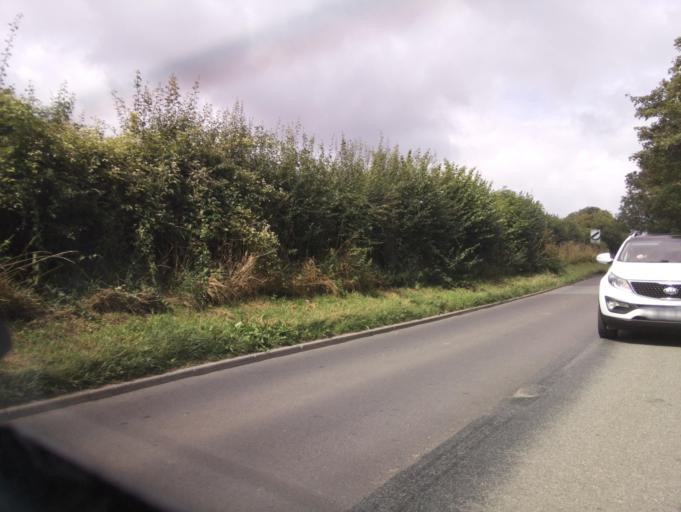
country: GB
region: England
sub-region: Somerset
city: Wincanton
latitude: 51.0069
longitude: -2.4211
